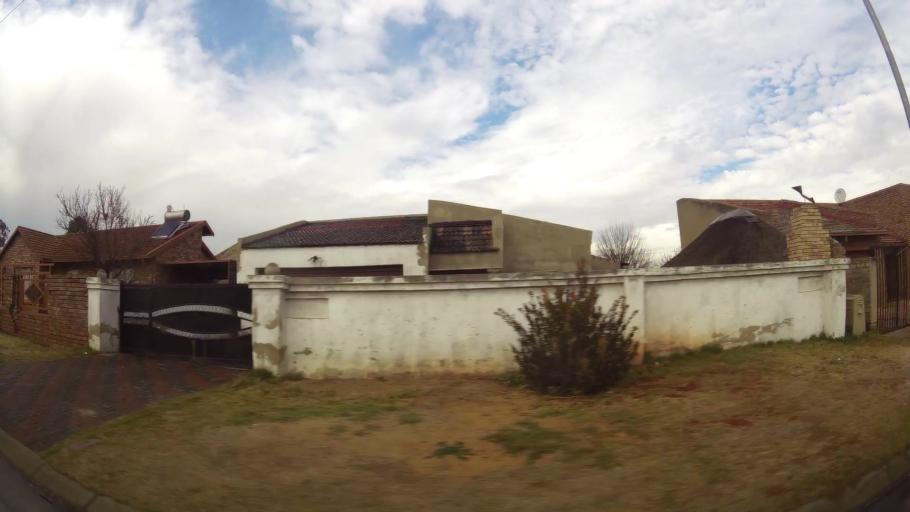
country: ZA
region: Gauteng
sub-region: Ekurhuleni Metropolitan Municipality
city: Germiston
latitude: -26.3310
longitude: 28.1892
